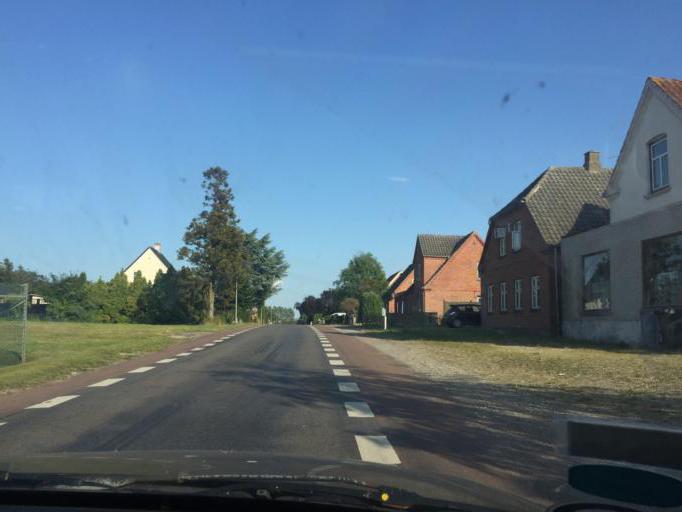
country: DK
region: Zealand
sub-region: Lolland Kommune
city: Maribo
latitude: 54.7977
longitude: 11.5225
